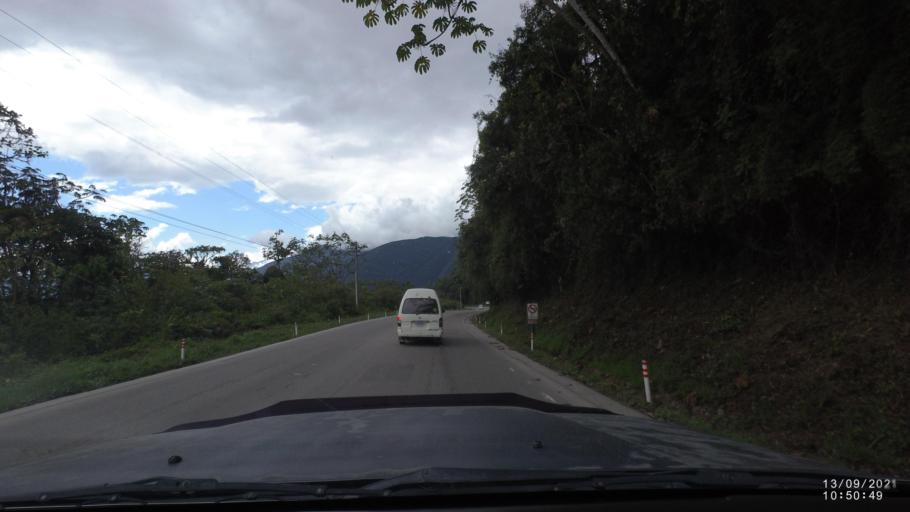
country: BO
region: Cochabamba
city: Colomi
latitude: -17.1970
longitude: -65.8486
